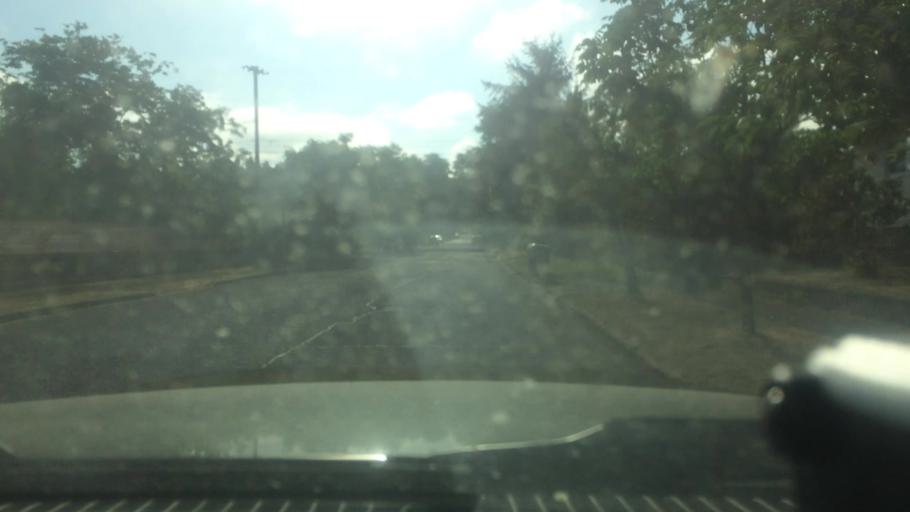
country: US
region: Oregon
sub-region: Lane County
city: Eugene
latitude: 44.0298
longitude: -123.1085
